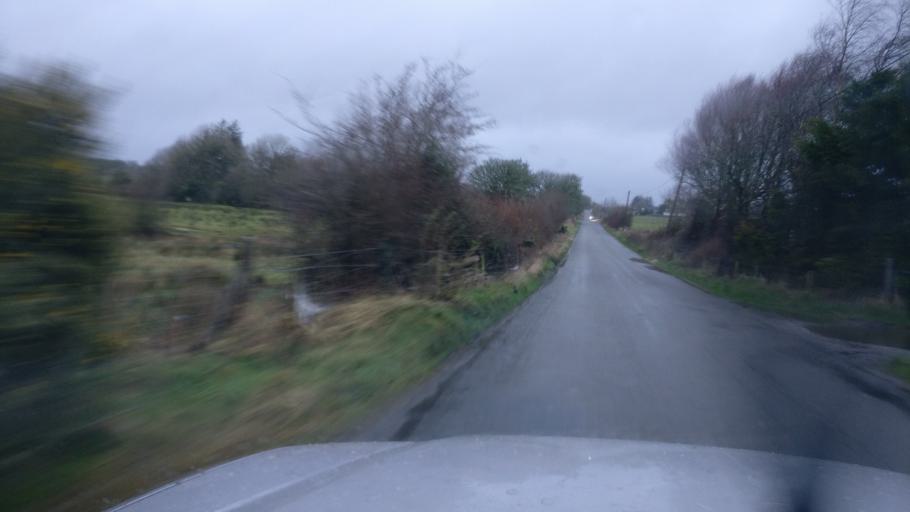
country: IE
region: Connaught
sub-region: County Galway
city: Loughrea
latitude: 53.2635
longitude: -8.4043
